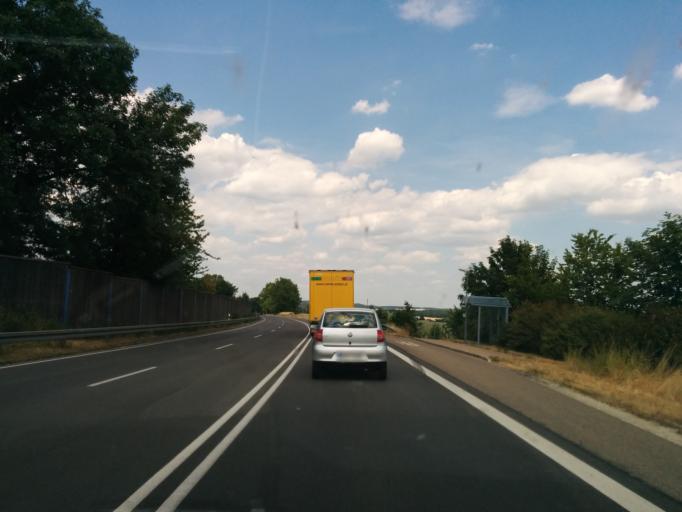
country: DE
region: Bavaria
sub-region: Swabia
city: Buchdorf
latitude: 48.7977
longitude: 10.8225
